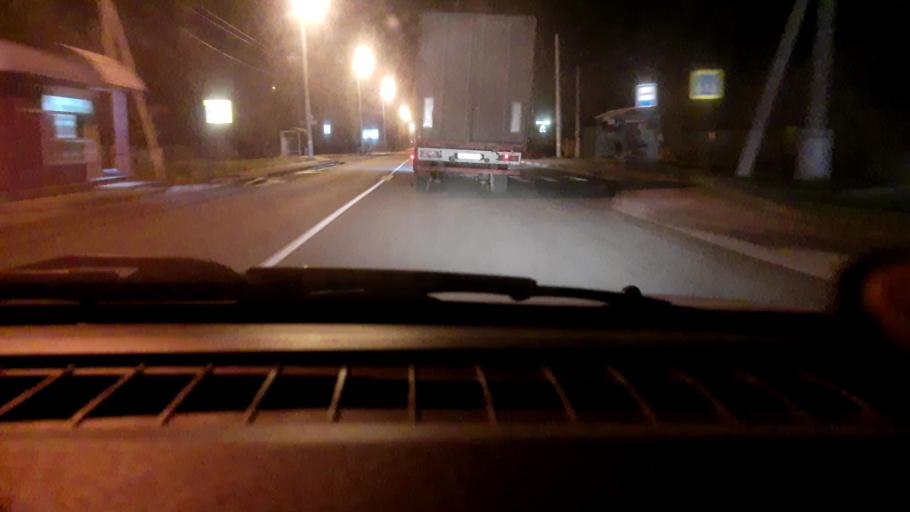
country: RU
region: Nizjnij Novgorod
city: Gorbatovka
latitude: 56.3832
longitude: 43.7871
